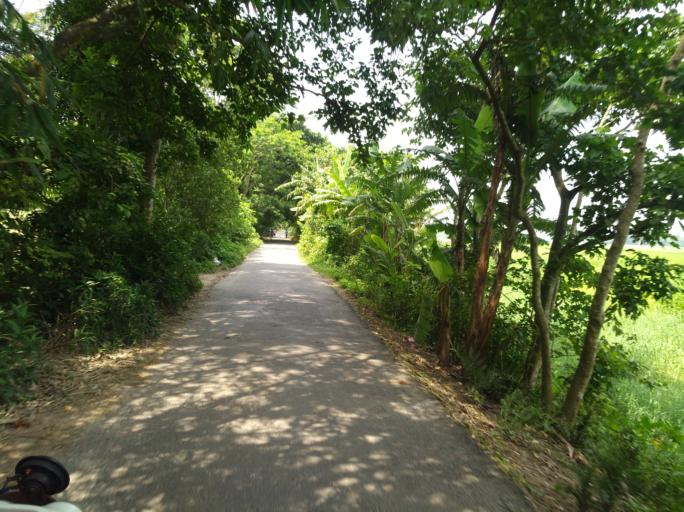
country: BD
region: Dhaka
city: Palang
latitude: 23.2500
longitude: 90.3096
